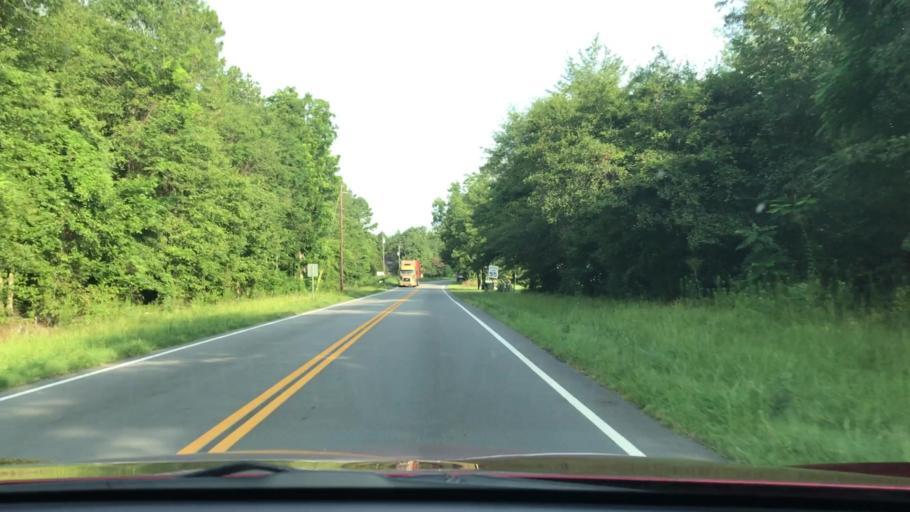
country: US
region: South Carolina
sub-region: Bamberg County
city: Denmark
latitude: 33.5338
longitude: -81.1295
